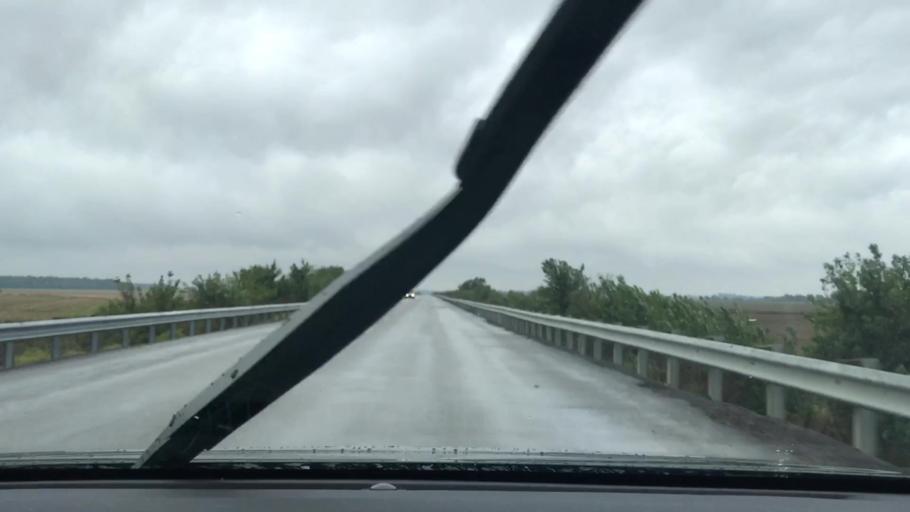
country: US
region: Kentucky
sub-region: McLean County
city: Calhoun
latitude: 37.3915
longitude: -87.3151
